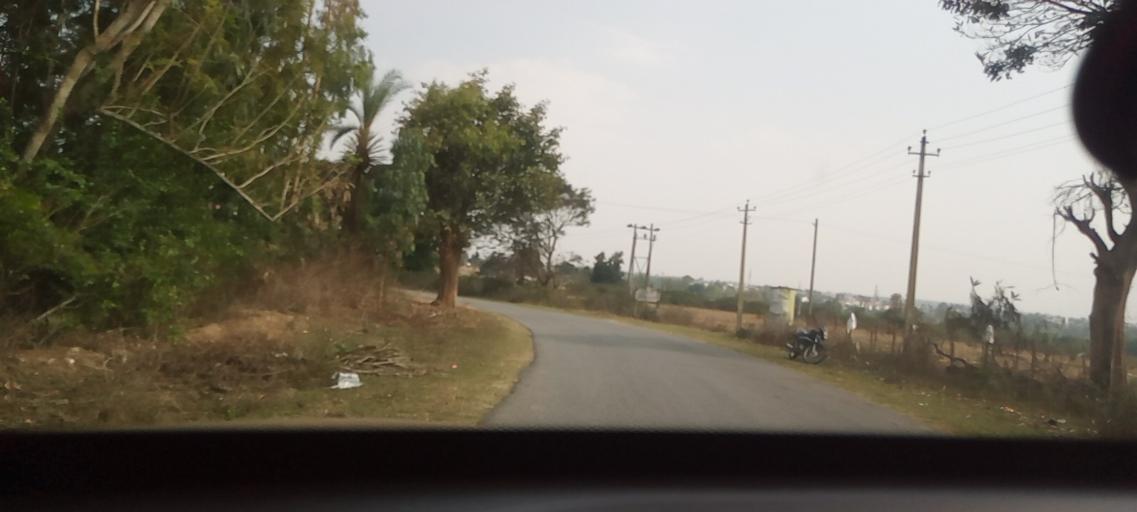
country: IN
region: Karnataka
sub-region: Hassan
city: Belur
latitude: 13.1772
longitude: 75.8476
